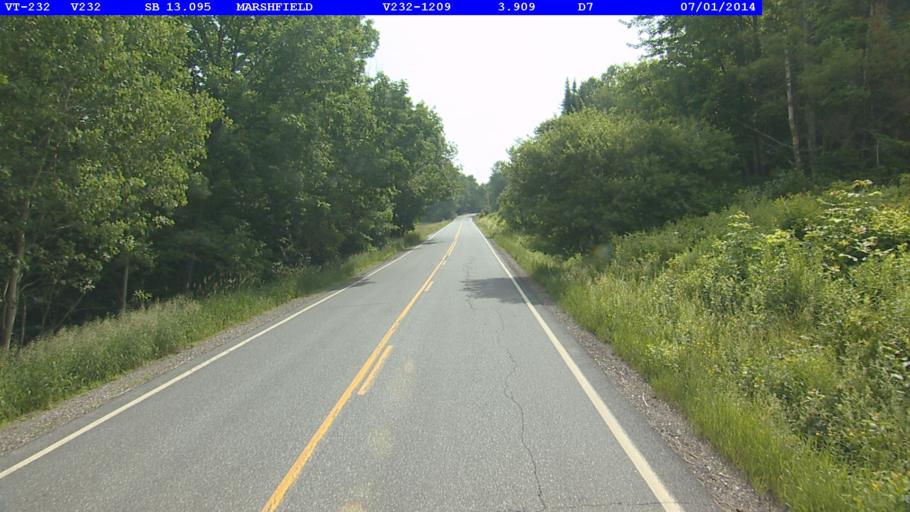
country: US
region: Vermont
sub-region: Caledonia County
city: Hardwick
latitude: 44.3582
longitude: -72.3204
